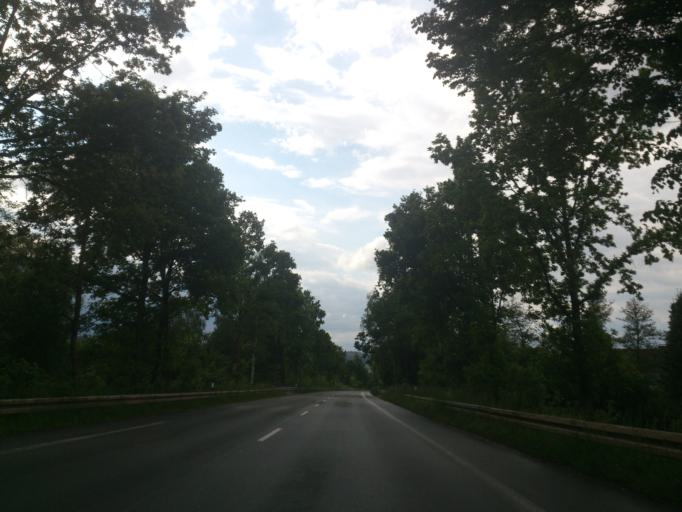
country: DE
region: North Rhine-Westphalia
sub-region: Regierungsbezirk Detmold
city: Willebadessen
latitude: 51.6201
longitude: 9.0290
